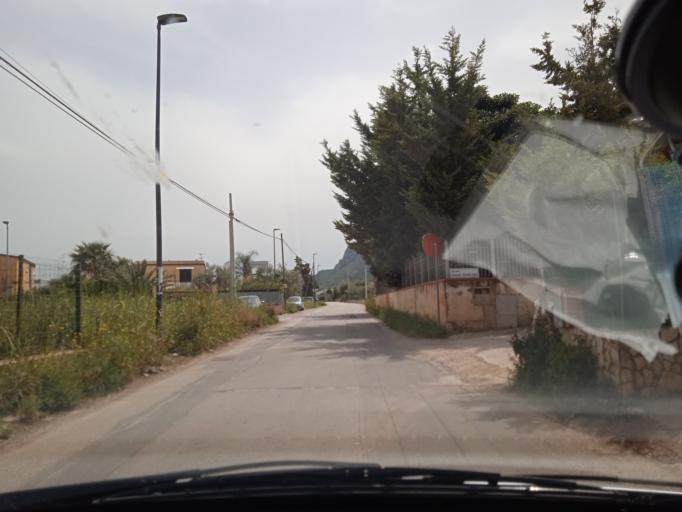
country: IT
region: Sicily
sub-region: Palermo
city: Torre Colonna-Sperone
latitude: 38.0324
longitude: 13.5656
